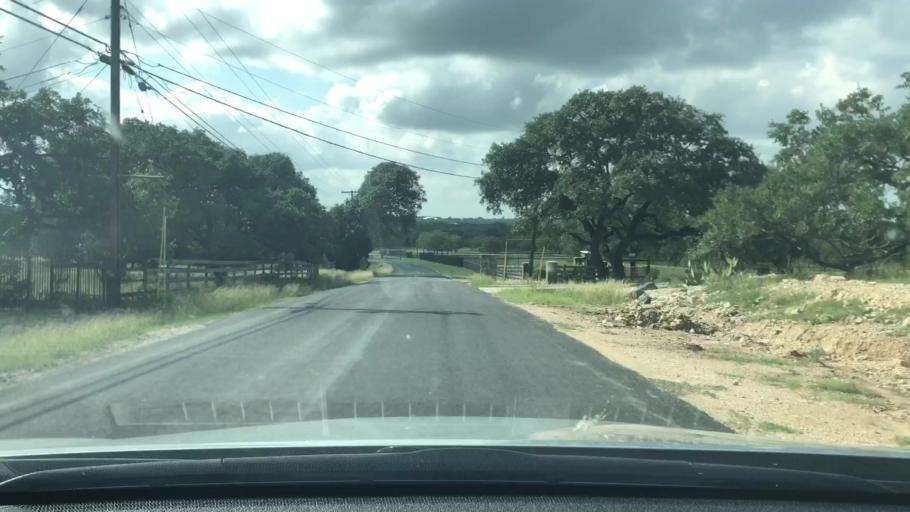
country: US
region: Texas
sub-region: Bexar County
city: Fair Oaks Ranch
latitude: 29.7677
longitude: -98.6295
